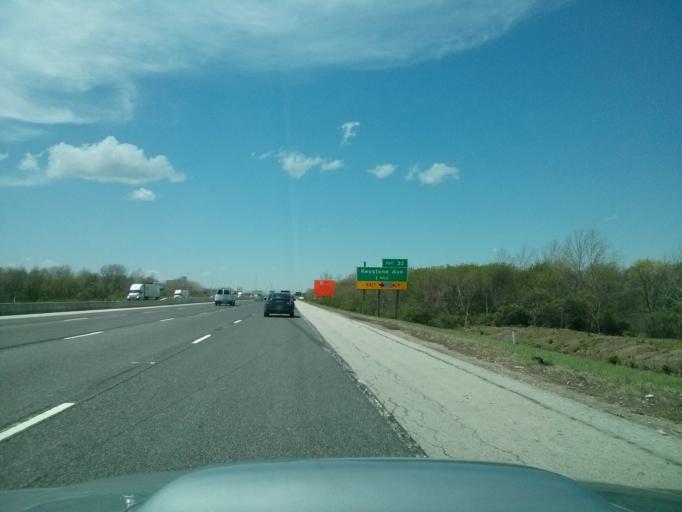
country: US
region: Indiana
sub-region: Hamilton County
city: Carmel
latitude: 39.9133
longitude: -86.0839
